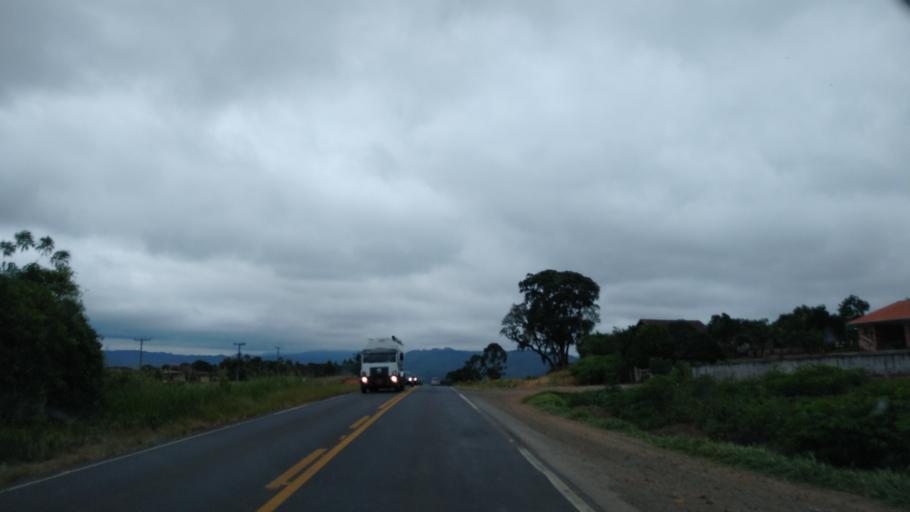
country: BR
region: Santa Catarina
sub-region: Porto Uniao
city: Porto Uniao
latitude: -26.2825
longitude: -51.0047
